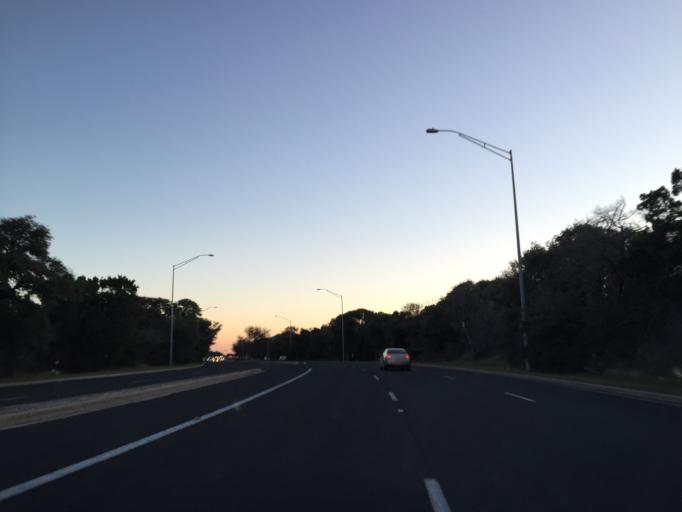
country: US
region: Texas
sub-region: Williamson County
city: Jollyville
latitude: 30.3974
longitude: -97.7401
